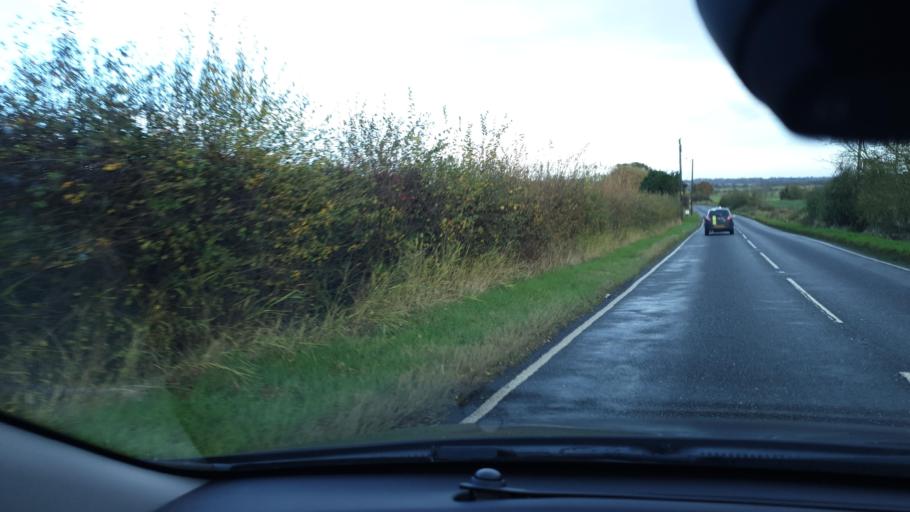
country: GB
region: England
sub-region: Essex
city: Little Clacton
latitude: 51.8616
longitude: 1.1741
